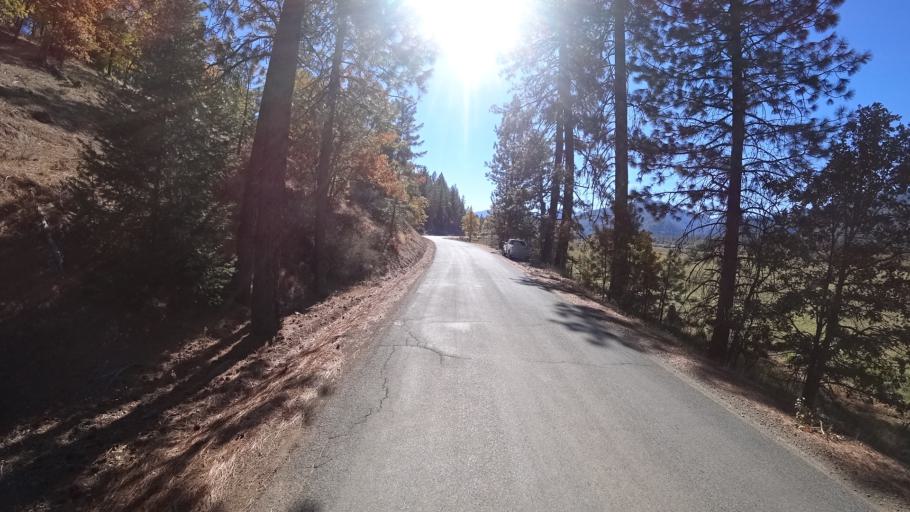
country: US
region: California
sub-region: Siskiyou County
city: Yreka
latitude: 41.6139
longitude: -122.9788
